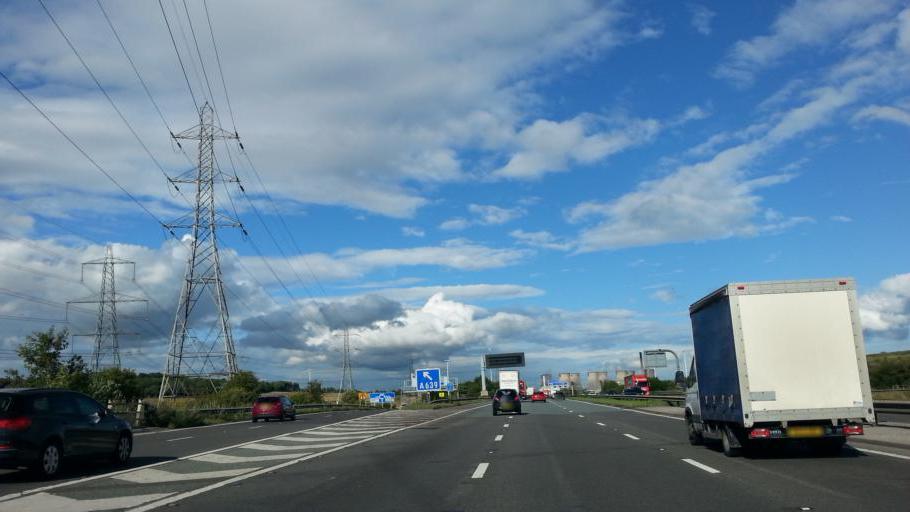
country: GB
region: England
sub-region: City and Borough of Wakefield
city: Pontefract
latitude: 53.7070
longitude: -1.3364
